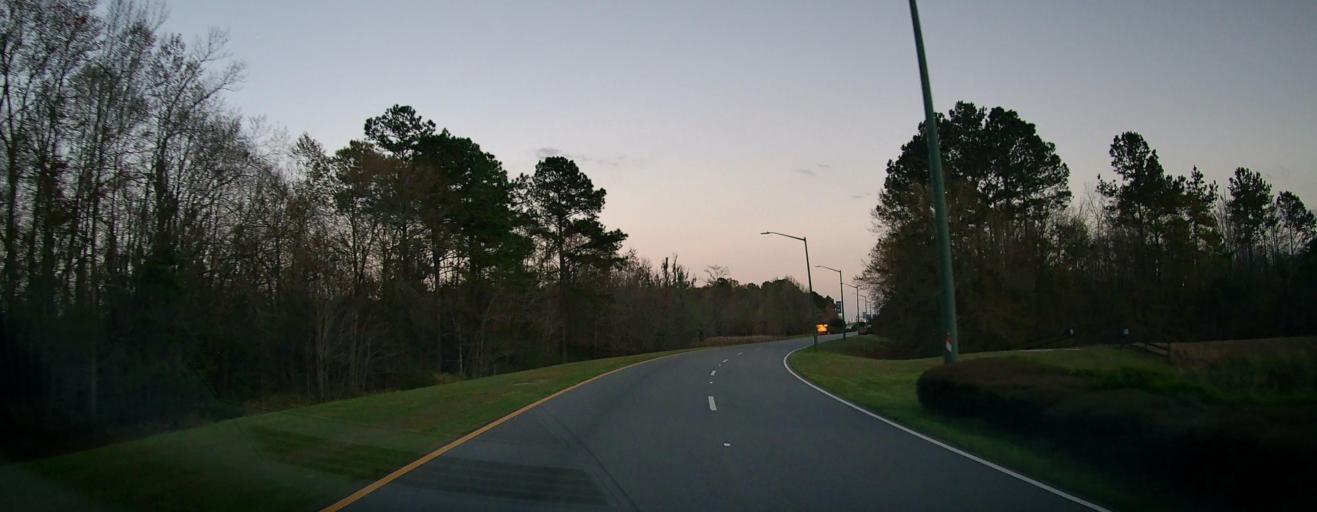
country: US
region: Georgia
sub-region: Chatham County
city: Pooler
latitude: 32.1375
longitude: -81.2191
